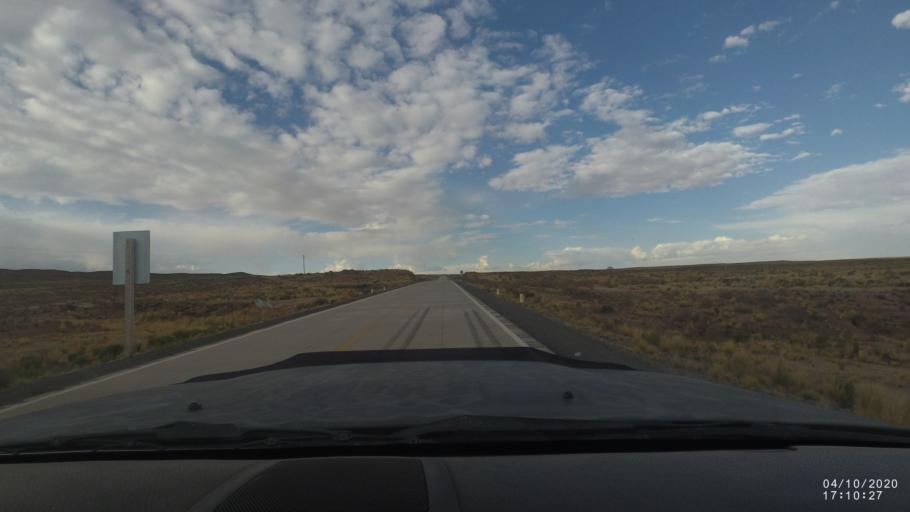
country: BO
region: Oruro
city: Oruro
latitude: -18.3310
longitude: -67.5840
